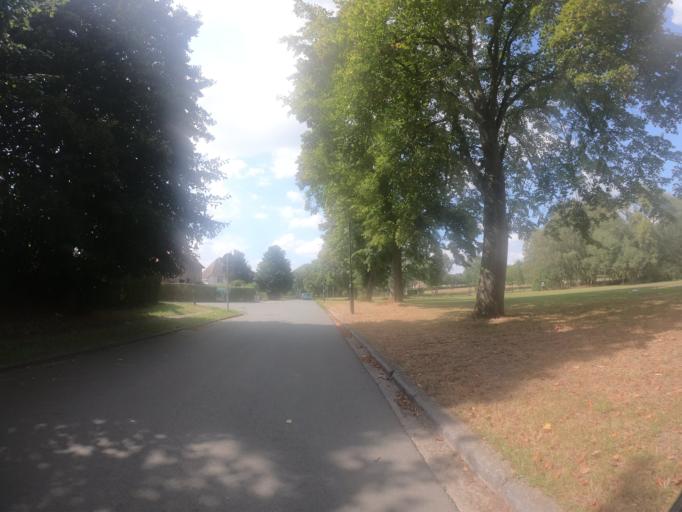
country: BE
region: Flanders
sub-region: Provincie Vlaams-Brabant
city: Dilbeek
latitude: 50.8380
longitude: 4.2757
